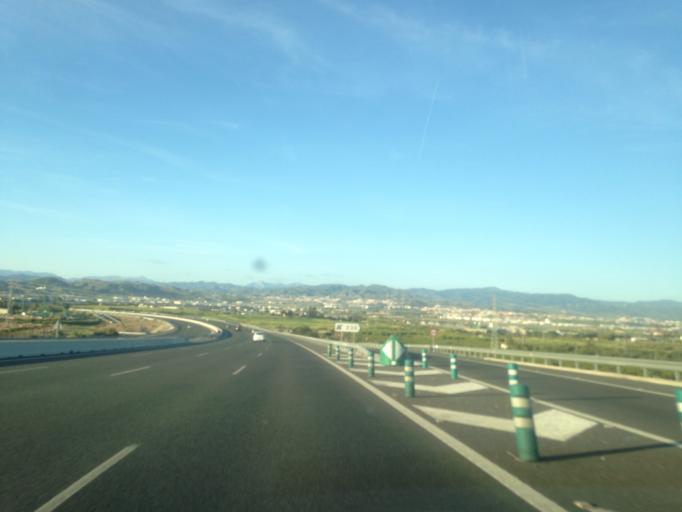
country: ES
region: Andalusia
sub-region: Provincia de Malaga
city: Alhaurin de la Torre
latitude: 36.6731
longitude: -4.5276
